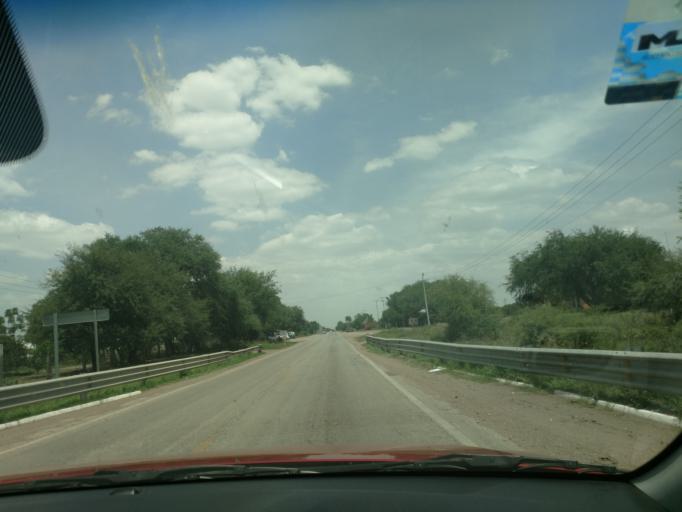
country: MX
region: San Luis Potosi
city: Ciudad Fernandez
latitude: 21.9554
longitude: -100.0710
